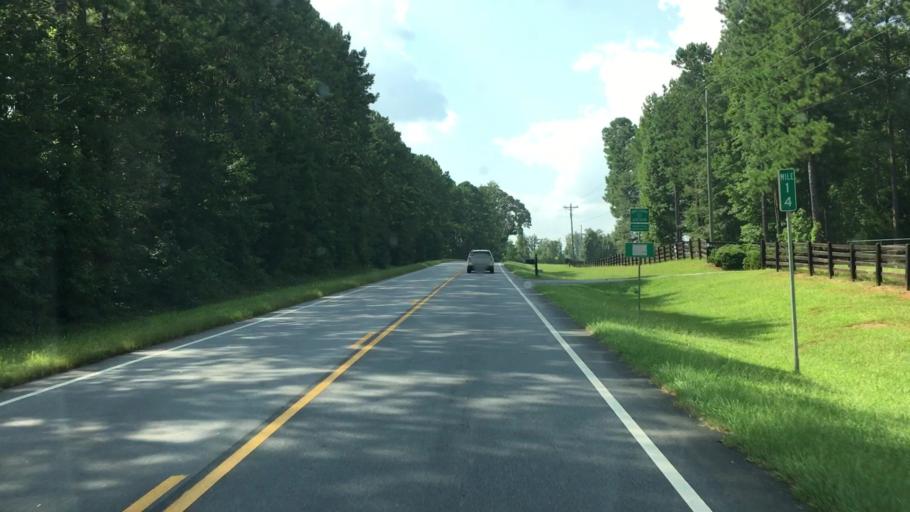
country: US
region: Georgia
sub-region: Jasper County
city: Monticello
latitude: 33.3294
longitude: -83.7081
